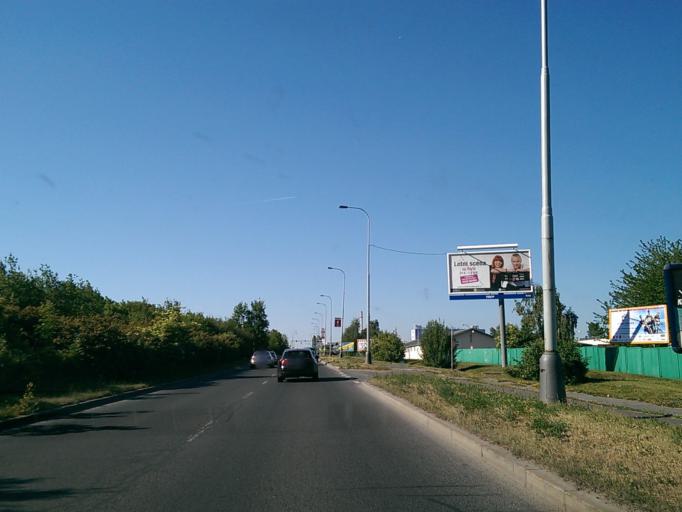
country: CZ
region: Praha
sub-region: Praha 14
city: Hostavice
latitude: 50.0588
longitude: 14.5372
